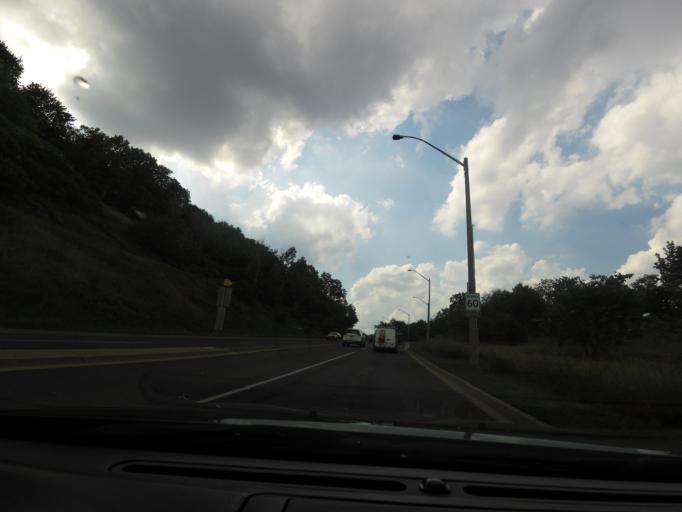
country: CA
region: Ontario
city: Hamilton
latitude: 43.2305
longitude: -79.8151
